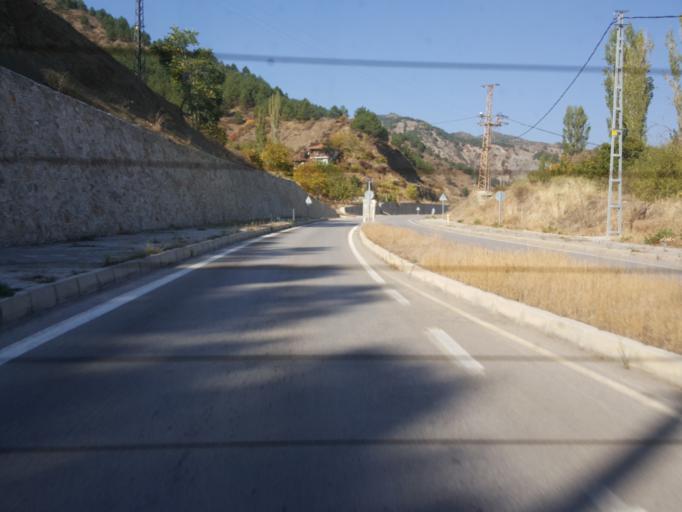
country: TR
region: Corum
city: Iskilip
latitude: 40.7373
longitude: 34.4529
